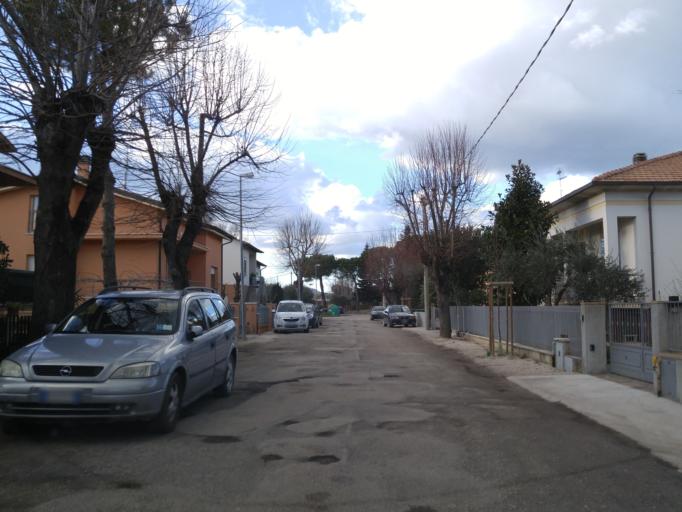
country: IT
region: The Marches
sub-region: Provincia di Pesaro e Urbino
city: Rosciano
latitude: 43.8260
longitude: 13.0010
